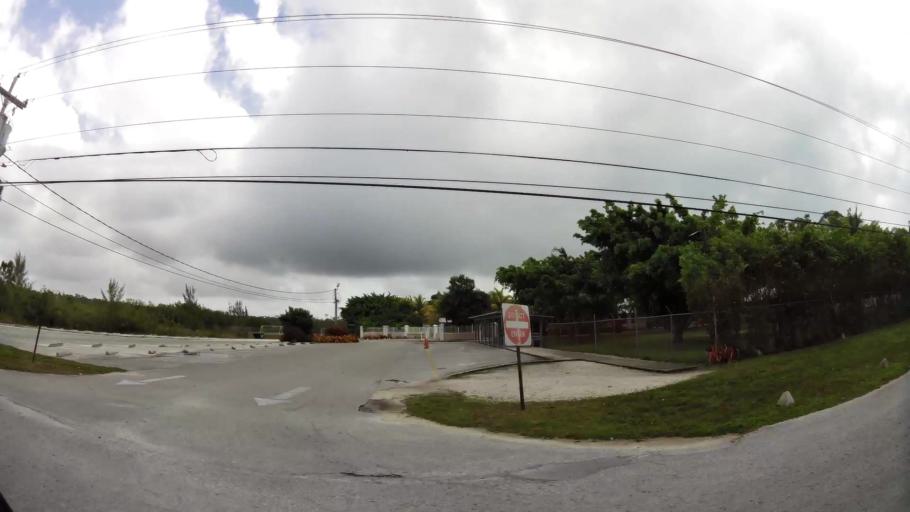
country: BS
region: Freeport
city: Lucaya
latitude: 26.5455
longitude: -78.5949
